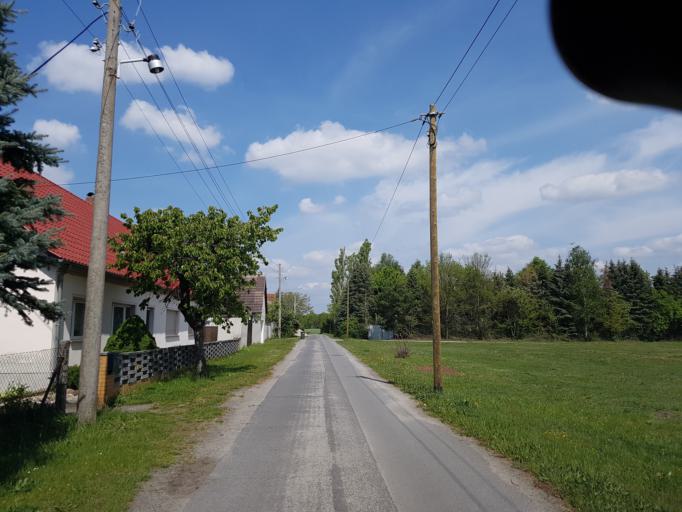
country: DE
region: Brandenburg
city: Finsterwalde
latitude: 51.5693
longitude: 13.6630
